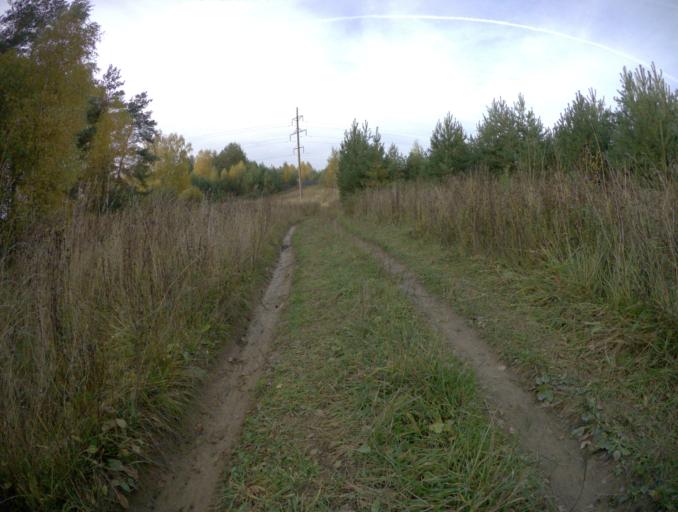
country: RU
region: Vladimir
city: Golovino
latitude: 56.0290
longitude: 40.4487
